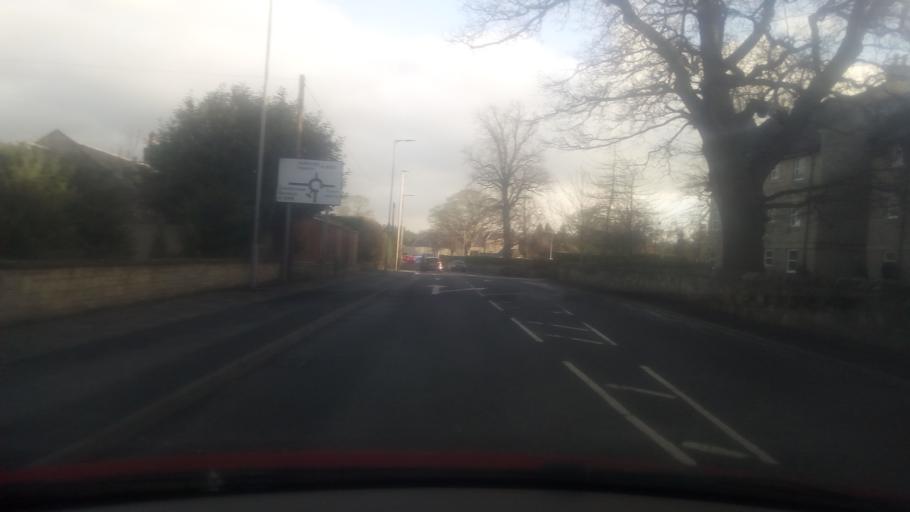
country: GB
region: Scotland
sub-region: The Scottish Borders
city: Kelso
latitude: 55.6022
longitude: -2.4278
